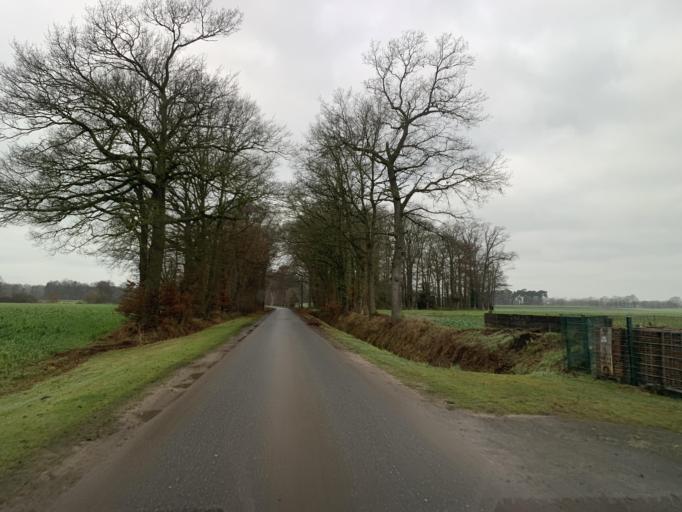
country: DE
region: North Rhine-Westphalia
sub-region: Regierungsbezirk Munster
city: Greven
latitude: 52.0669
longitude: 7.5617
